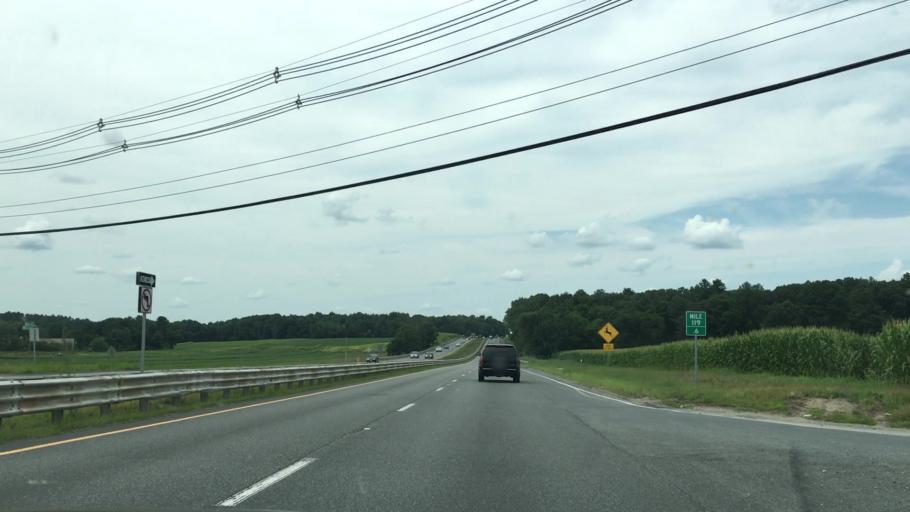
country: US
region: Massachusetts
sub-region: Middlesex County
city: West Concord
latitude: 42.4701
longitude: -71.4124
